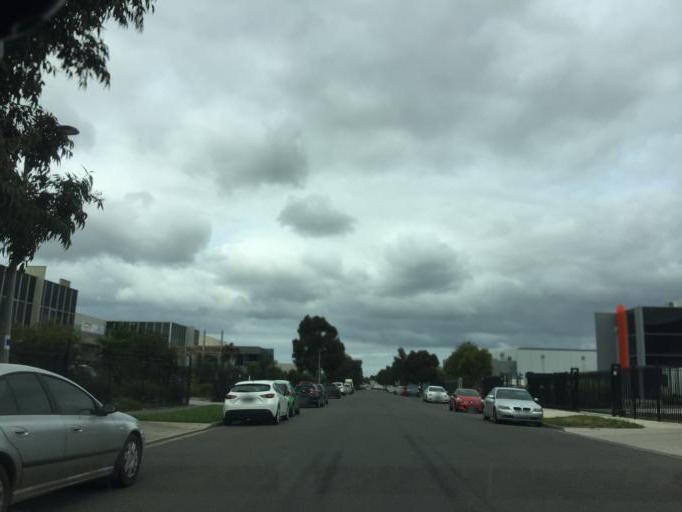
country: AU
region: Victoria
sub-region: Brimbank
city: Brooklyn
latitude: -37.8122
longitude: 144.8214
